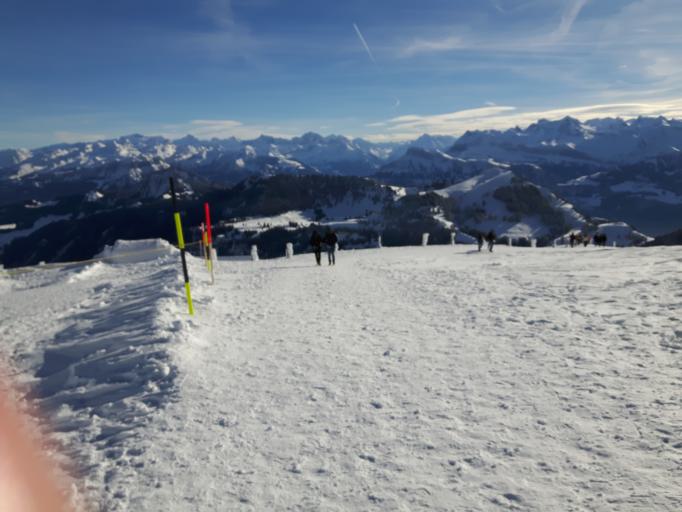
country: CH
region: Schwyz
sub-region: Bezirk Schwyz
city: Arth
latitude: 47.0565
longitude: 8.4865
